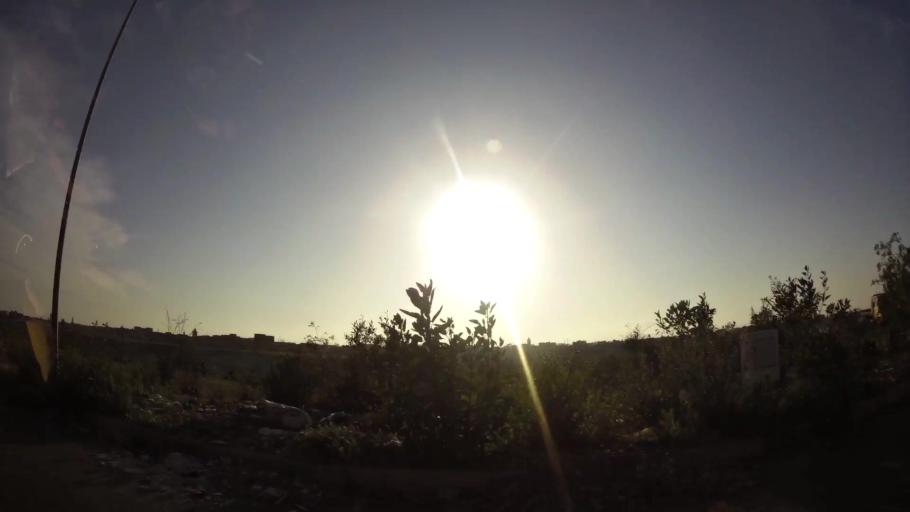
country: MA
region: Oriental
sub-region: Oujda-Angad
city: Oujda
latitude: 34.7096
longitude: -1.9023
